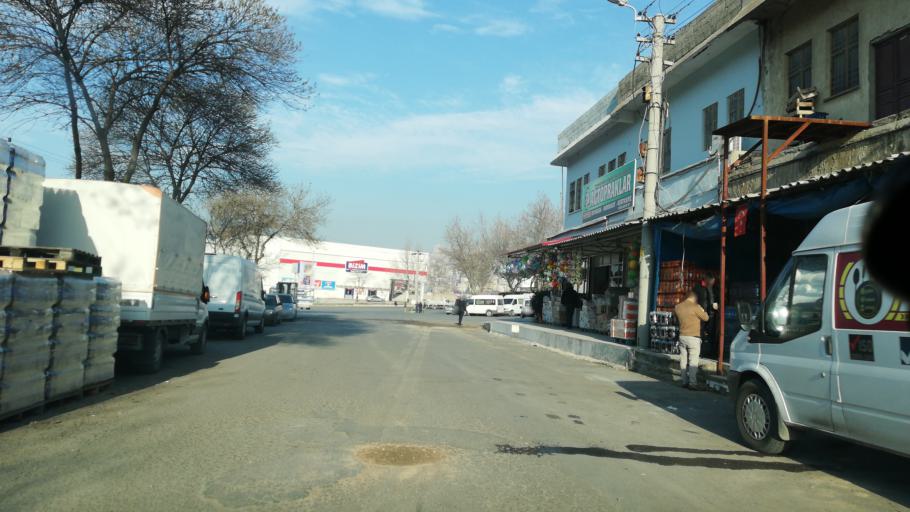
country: TR
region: Kahramanmaras
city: Kahramanmaras
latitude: 37.5653
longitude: 36.9183
